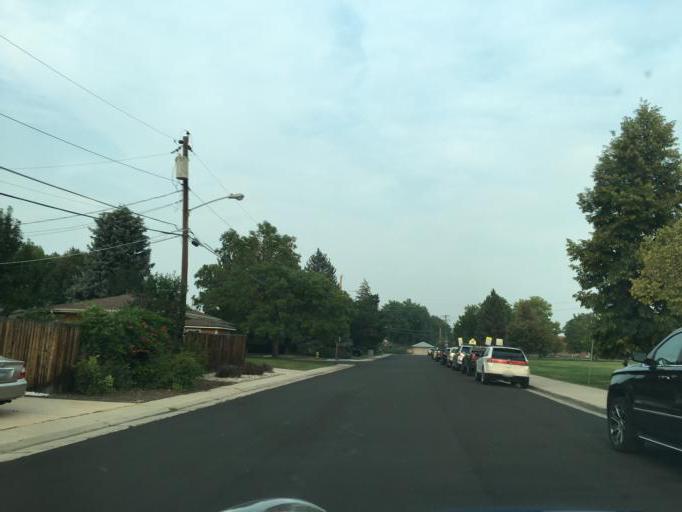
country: US
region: Colorado
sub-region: Arapahoe County
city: Glendale
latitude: 39.6859
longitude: -104.9243
